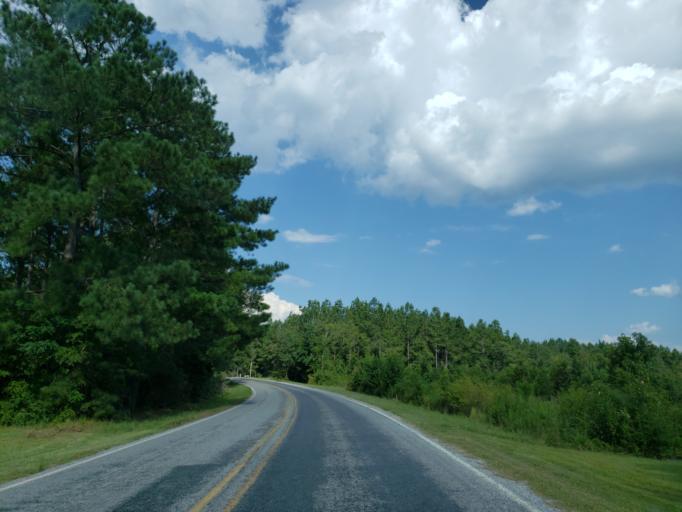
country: US
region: Mississippi
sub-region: Covington County
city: Collins
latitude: 31.6189
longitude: -89.3887
